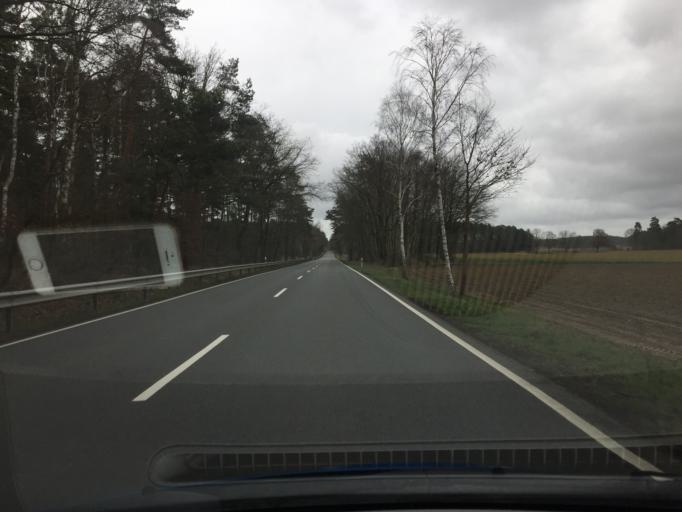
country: DE
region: Lower Saxony
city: Stoetze
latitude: 53.0404
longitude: 10.7915
